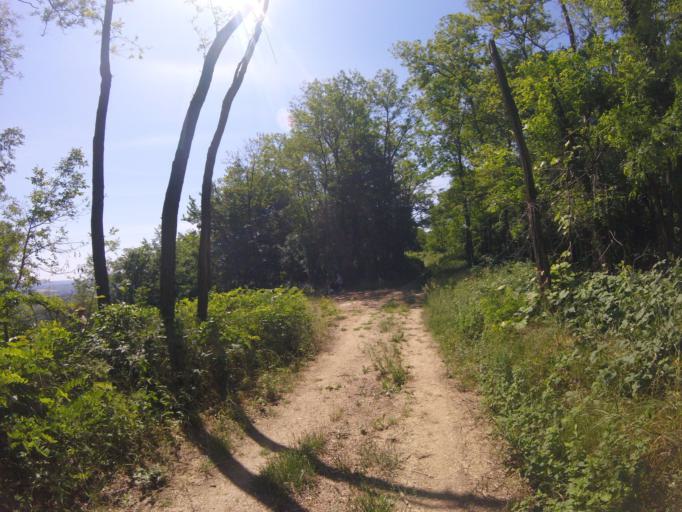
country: HU
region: Zala
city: Zalaszentgrot
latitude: 46.9210
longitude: 17.0442
